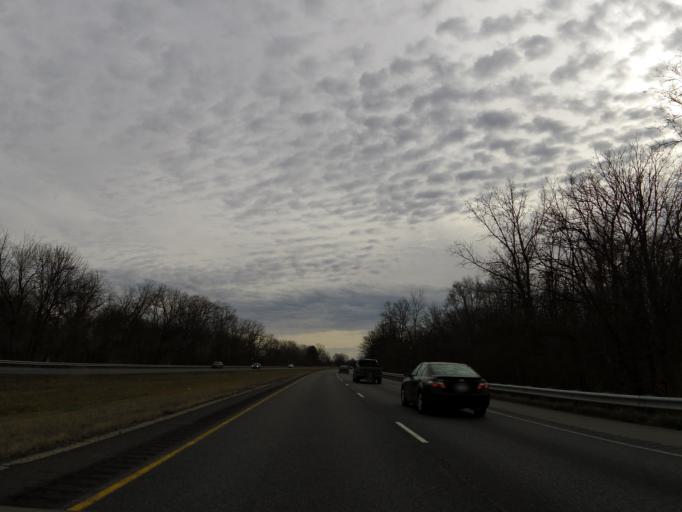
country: US
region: Indiana
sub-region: Hendricks County
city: Pittsboro
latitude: 39.8791
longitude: -86.4390
